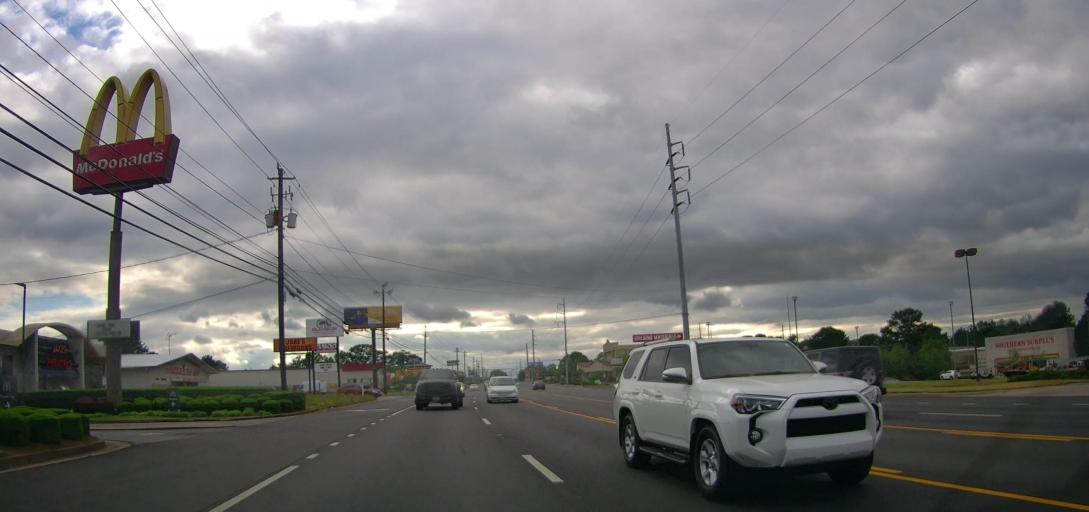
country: US
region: Georgia
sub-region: Oconee County
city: Bogart
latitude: 33.9406
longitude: -83.4717
